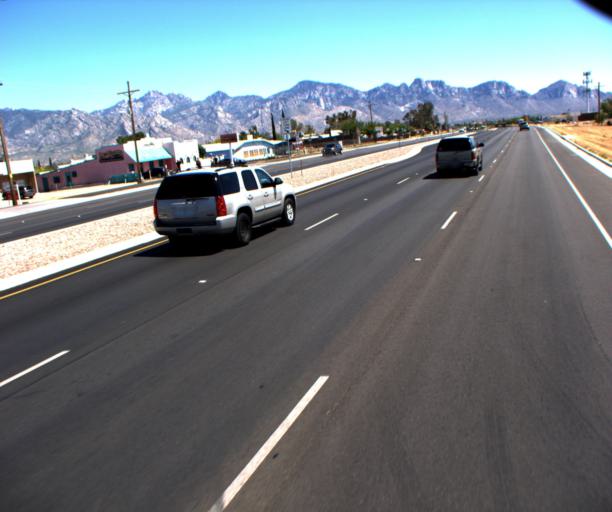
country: US
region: Arizona
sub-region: Pima County
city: Catalina
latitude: 32.5017
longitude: -110.9262
